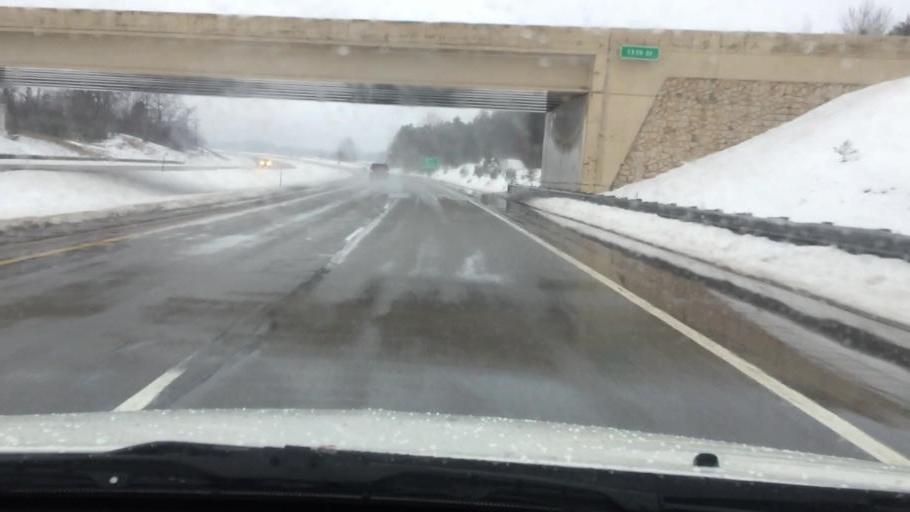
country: US
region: Michigan
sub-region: Wexford County
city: Cadillac
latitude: 44.2671
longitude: -85.3880
